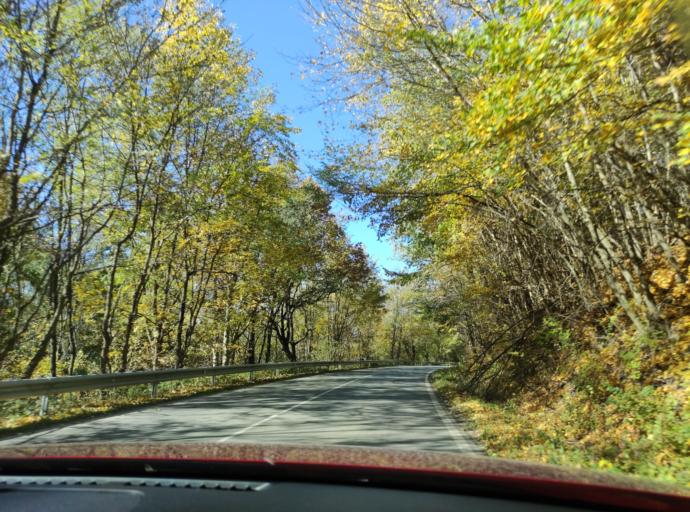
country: BG
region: Montana
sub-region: Obshtina Montana
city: Montana
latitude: 43.4071
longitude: 23.0526
